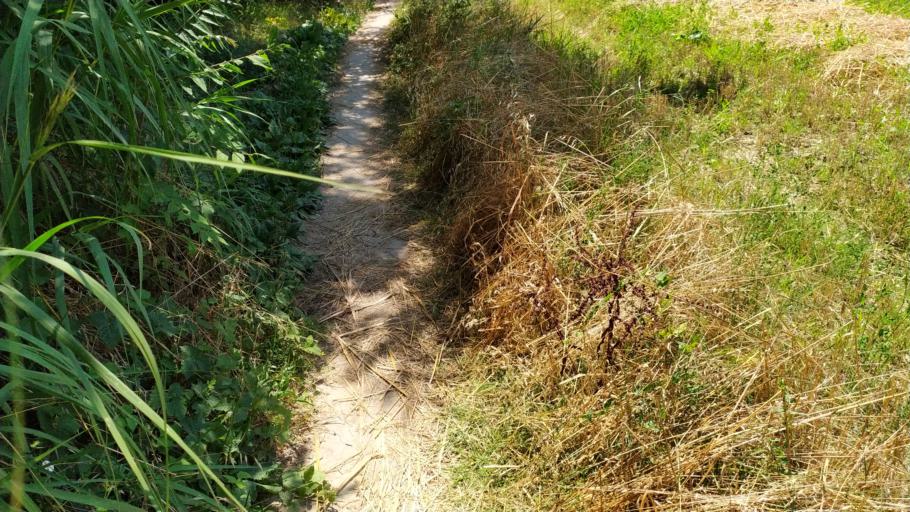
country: IT
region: Emilia-Romagna
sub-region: Forli-Cesena
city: Castrocaro Terme e Terra del Sole
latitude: 44.1897
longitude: 11.9690
